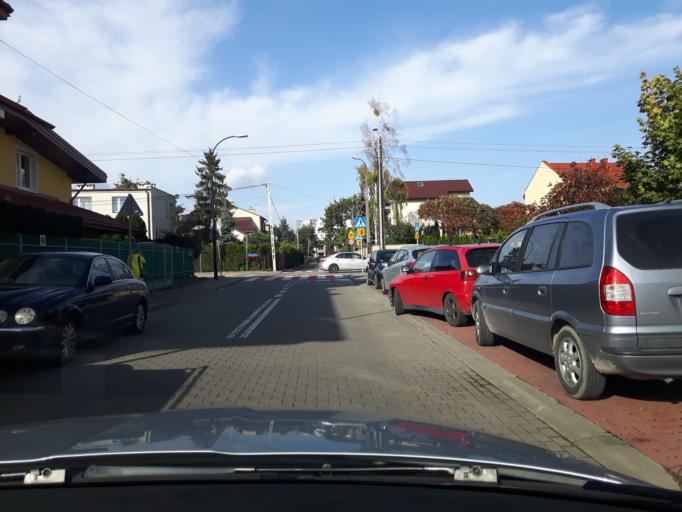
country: PL
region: Masovian Voivodeship
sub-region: Powiat wolominski
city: Zabki
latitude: 52.2846
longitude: 21.0805
